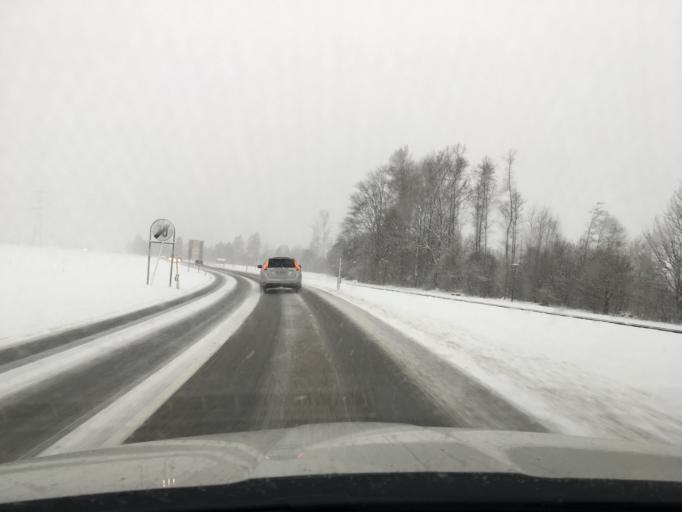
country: AT
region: Tyrol
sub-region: Politischer Bezirk Schwaz
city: Schwendau
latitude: 47.1888
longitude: 11.8668
